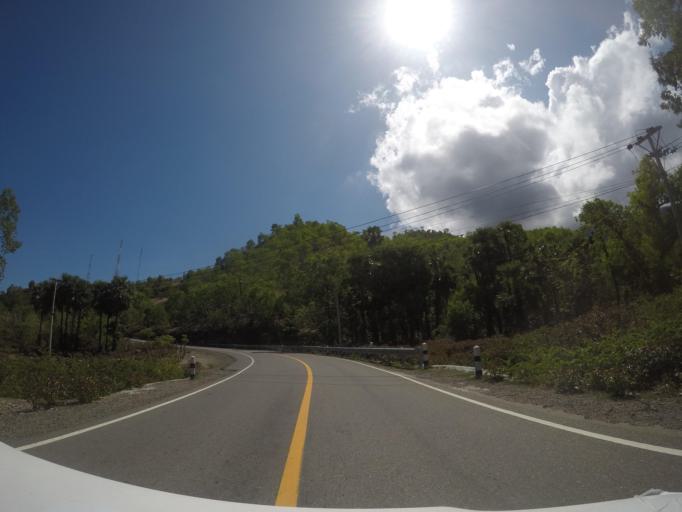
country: ID
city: Metinaro
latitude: -8.4833
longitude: 125.8427
